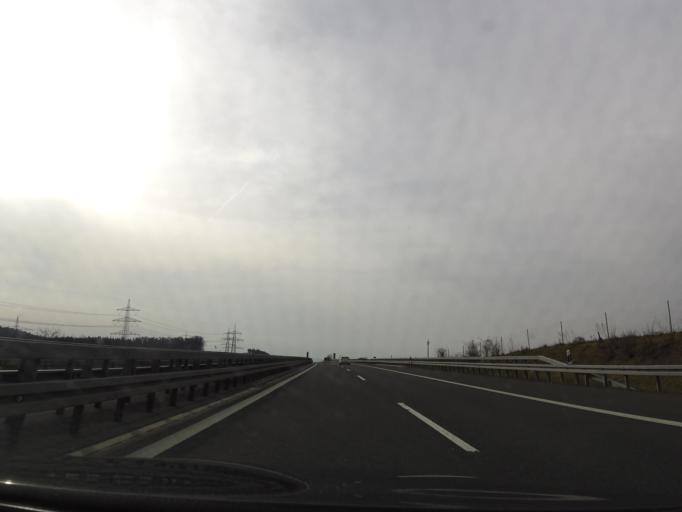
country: DE
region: Bavaria
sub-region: Upper Franconia
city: Rodental
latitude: 50.2586
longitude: 11.0206
